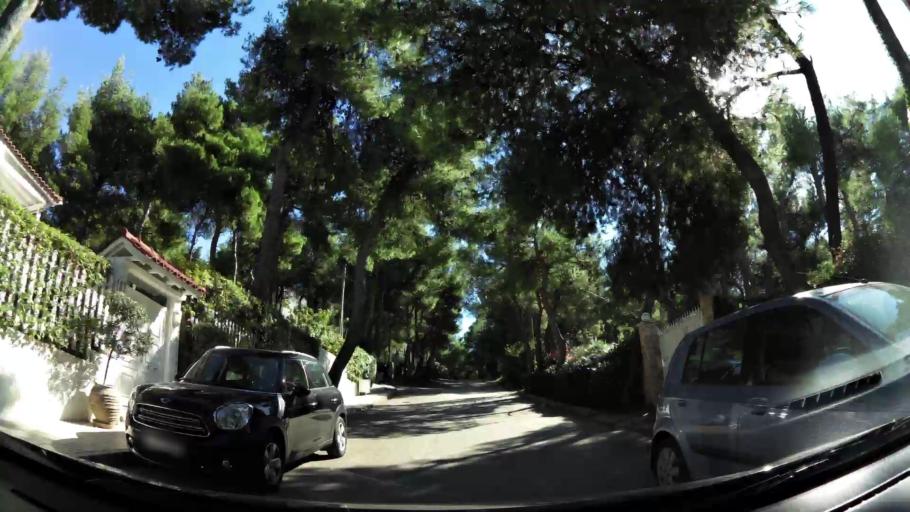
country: GR
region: Attica
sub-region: Nomarchia Anatolikis Attikis
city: Dionysos
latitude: 38.1053
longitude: 23.8855
